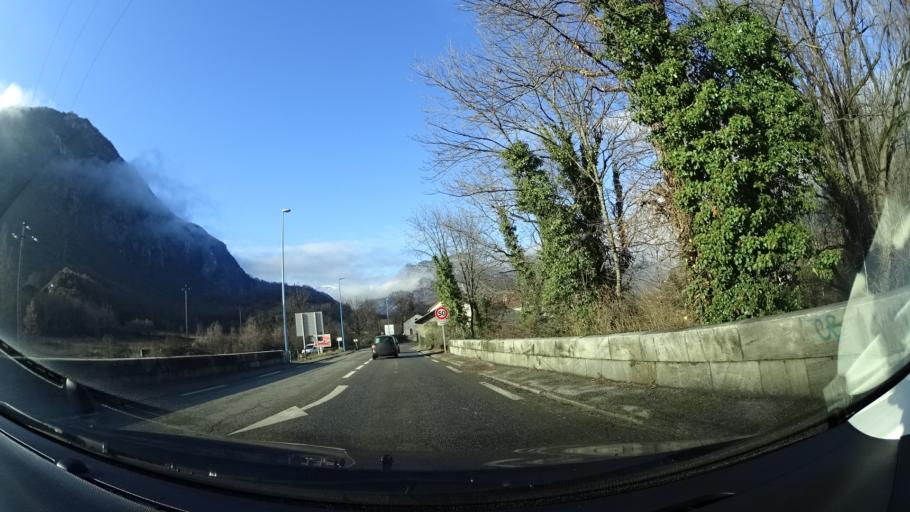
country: FR
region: Midi-Pyrenees
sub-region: Departement de l'Ariege
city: Tarascon-sur-Ariege
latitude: 42.8383
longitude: 1.6035
